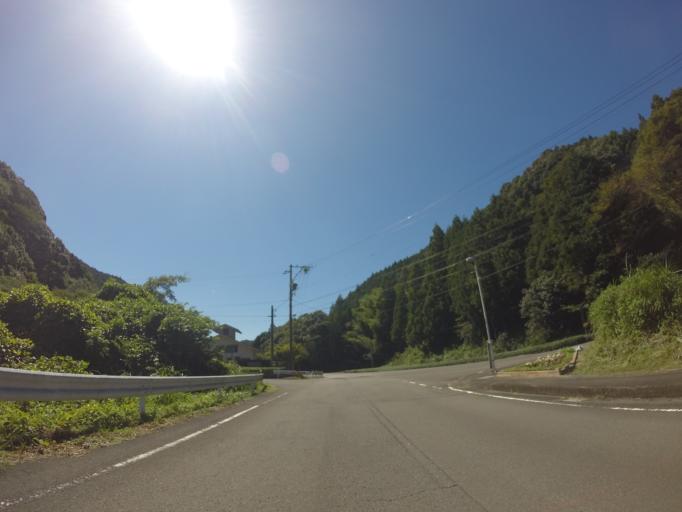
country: JP
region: Shizuoka
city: Fujieda
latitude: 34.9640
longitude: 138.2122
